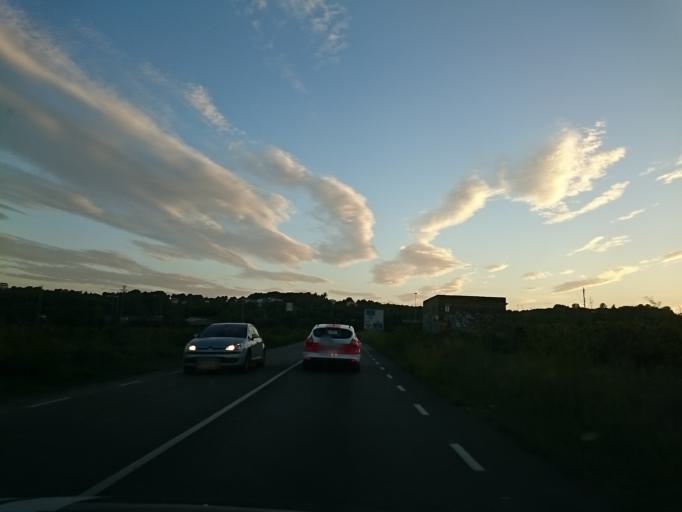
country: ES
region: Catalonia
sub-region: Provincia de Barcelona
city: Sant Pere de Ribes
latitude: 41.2443
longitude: 1.7676
